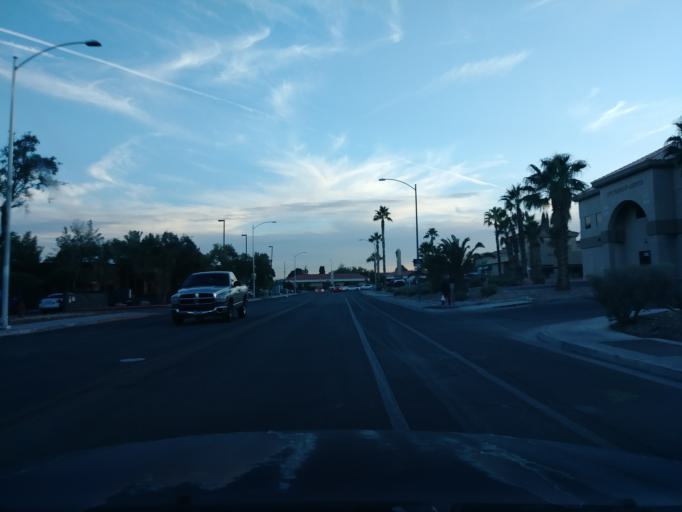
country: US
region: Nevada
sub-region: Clark County
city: Spring Valley
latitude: 36.1605
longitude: -115.2420
